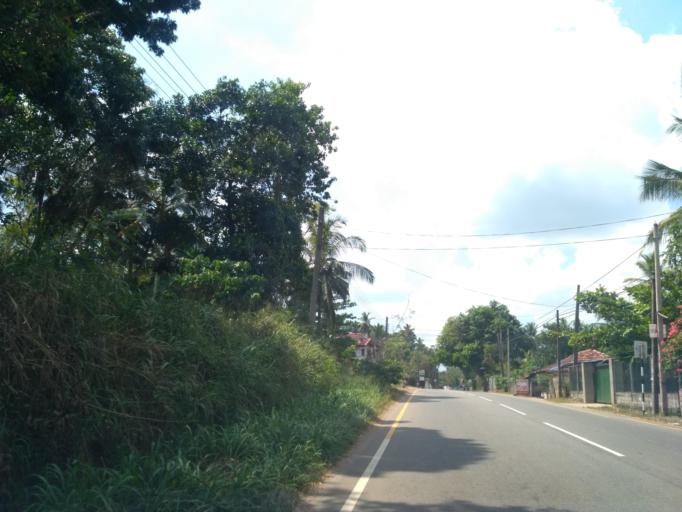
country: LK
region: North Western
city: Kuliyapitiya
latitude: 7.3270
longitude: 80.0544
